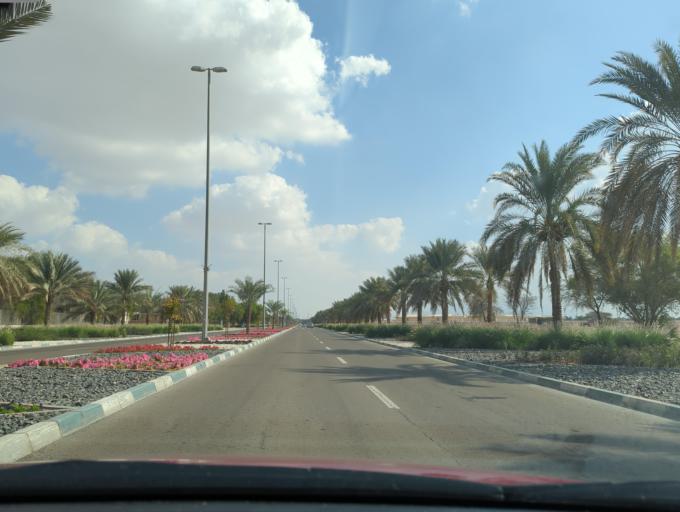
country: AE
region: Abu Dhabi
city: Al Ain
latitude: 24.1847
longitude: 55.6386
